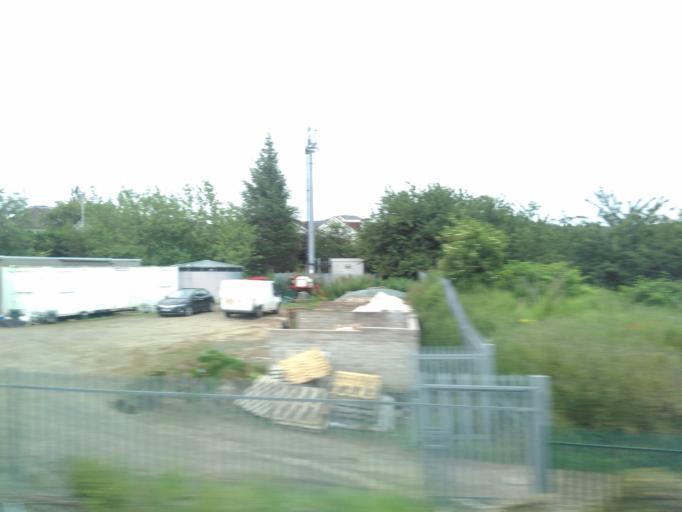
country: GB
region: Scotland
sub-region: Edinburgh
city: Colinton
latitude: 55.9186
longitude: -3.2659
